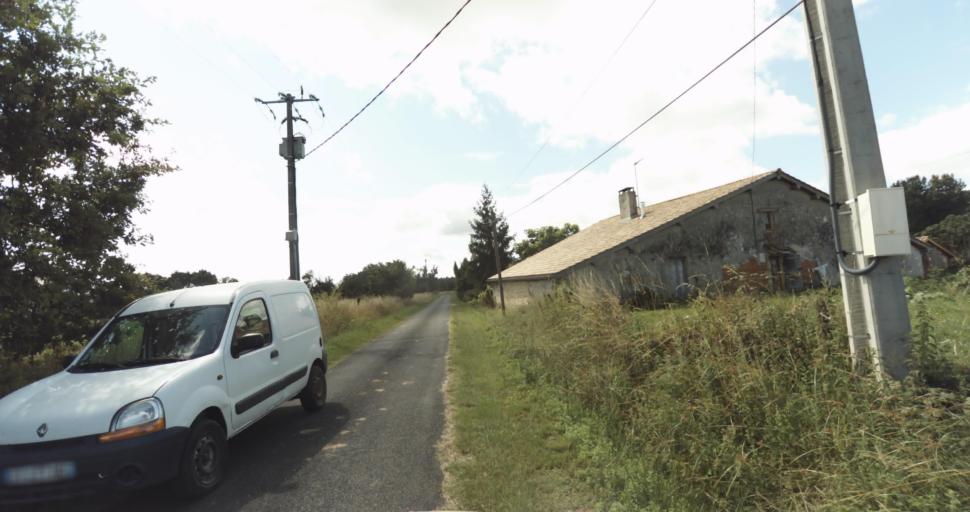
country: FR
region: Aquitaine
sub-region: Departement de la Gironde
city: Bazas
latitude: 44.4561
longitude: -0.2189
